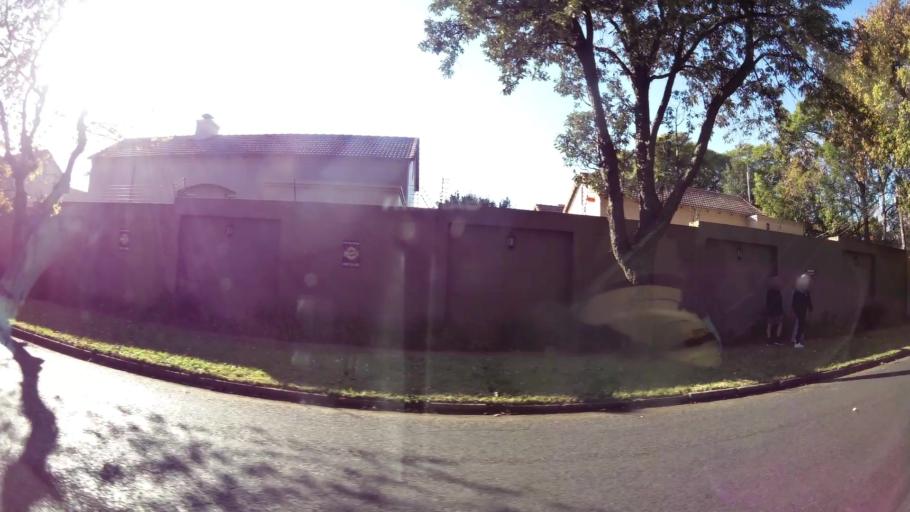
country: ZA
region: Gauteng
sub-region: City of Johannesburg Metropolitan Municipality
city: Johannesburg
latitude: -26.1576
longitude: 28.0653
